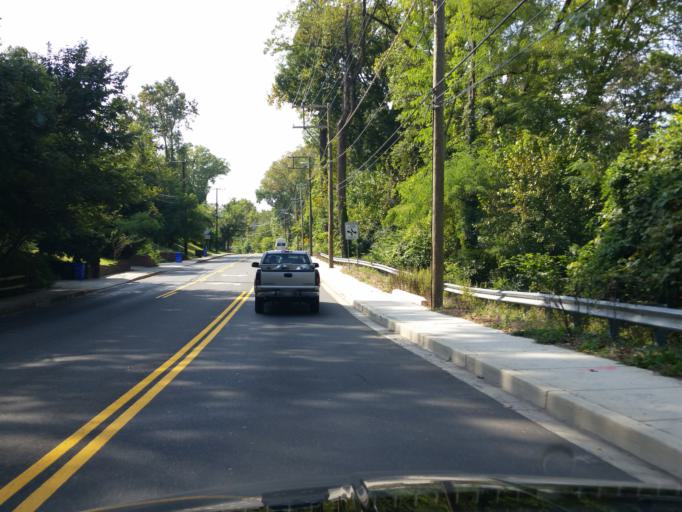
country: US
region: Maryland
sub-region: Montgomery County
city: Takoma Park
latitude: 38.9957
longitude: -77.0064
